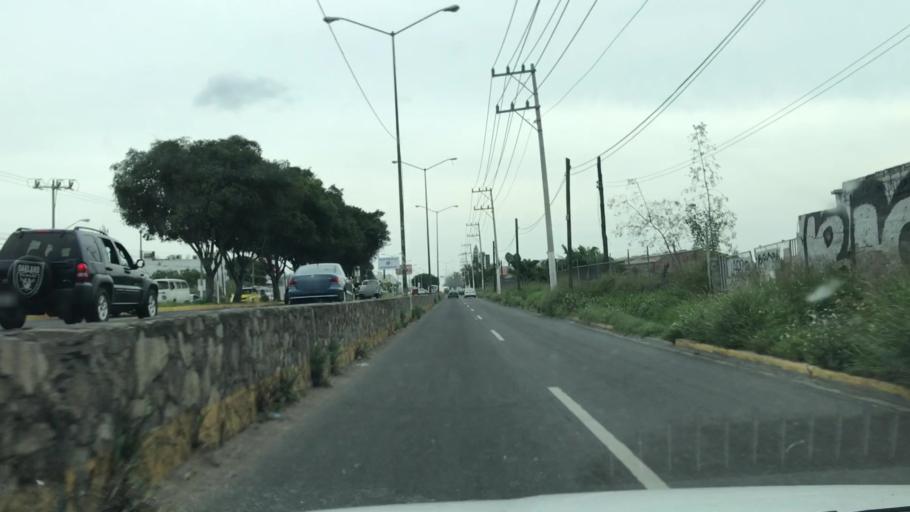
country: MX
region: Jalisco
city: Nuevo Mexico
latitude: 20.7522
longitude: -103.4228
